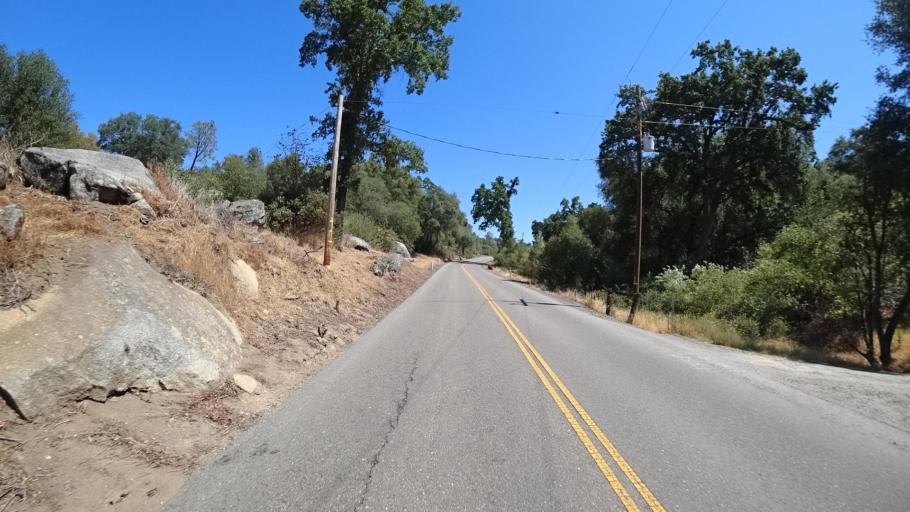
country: US
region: California
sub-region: Mariposa County
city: Mariposa
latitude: 37.4419
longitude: -119.9403
